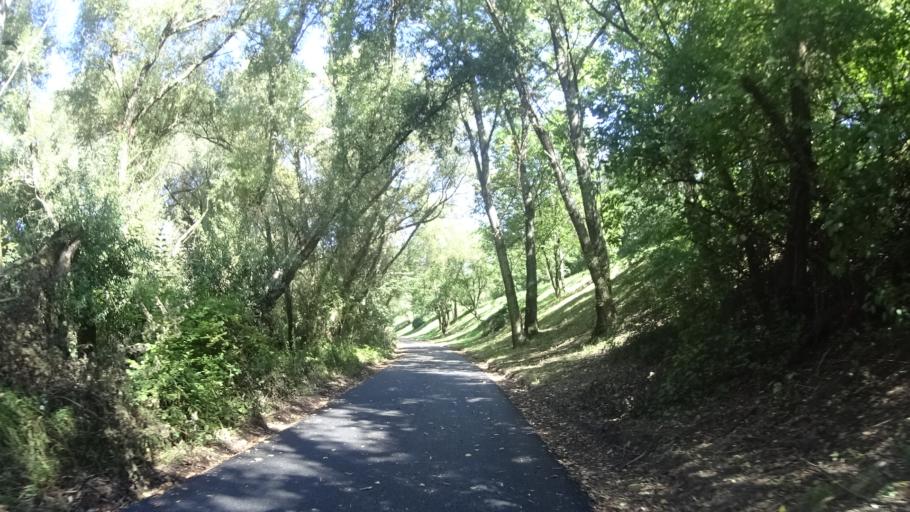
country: AT
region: Lower Austria
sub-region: Politischer Bezirk Bruck an der Leitha
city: Hainburg an der Donau
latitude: 48.1899
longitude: 16.9773
